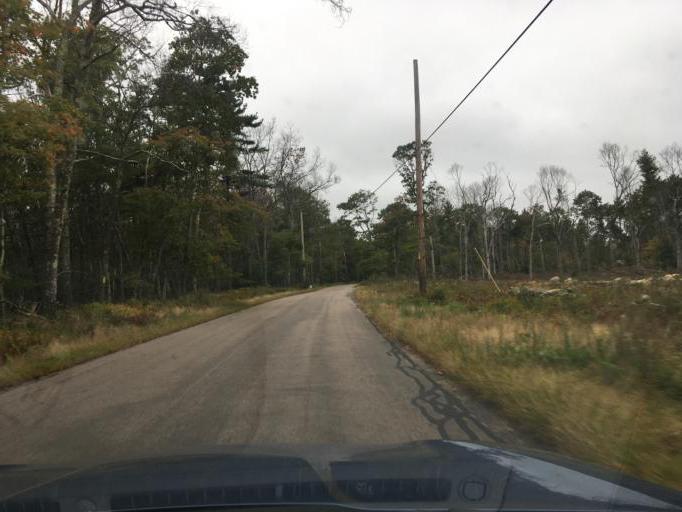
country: US
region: Rhode Island
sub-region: Washington County
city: Exeter
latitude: 41.5941
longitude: -71.5644
